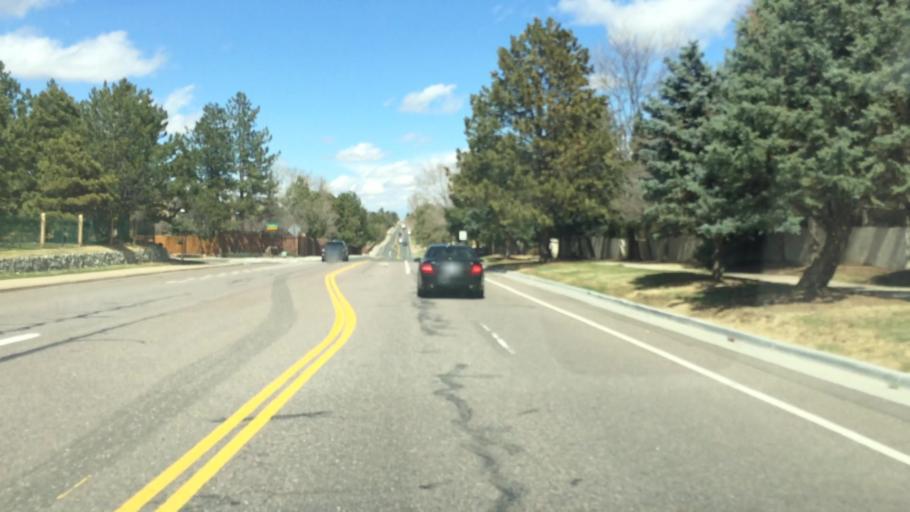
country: US
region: Colorado
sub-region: Arapahoe County
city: Centennial
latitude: 39.6052
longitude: -104.8761
